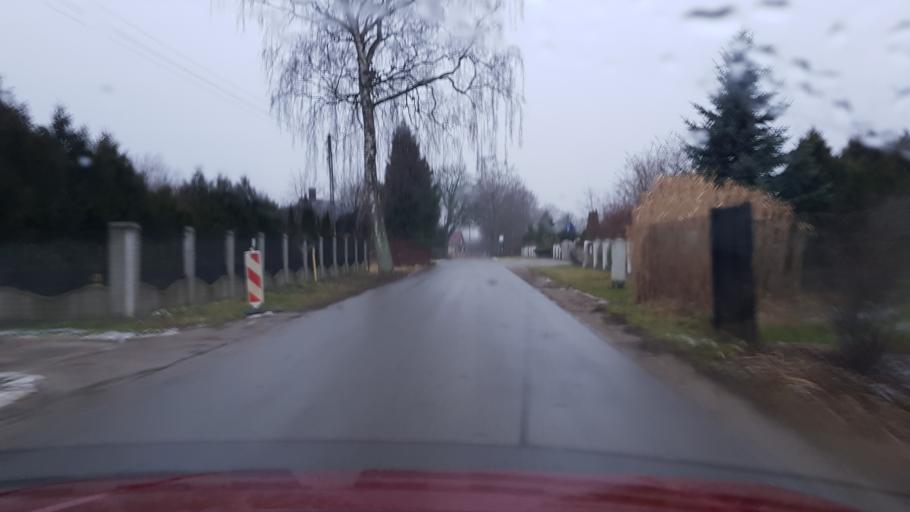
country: PL
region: West Pomeranian Voivodeship
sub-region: Koszalin
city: Koszalin
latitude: 54.1753
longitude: 16.2371
